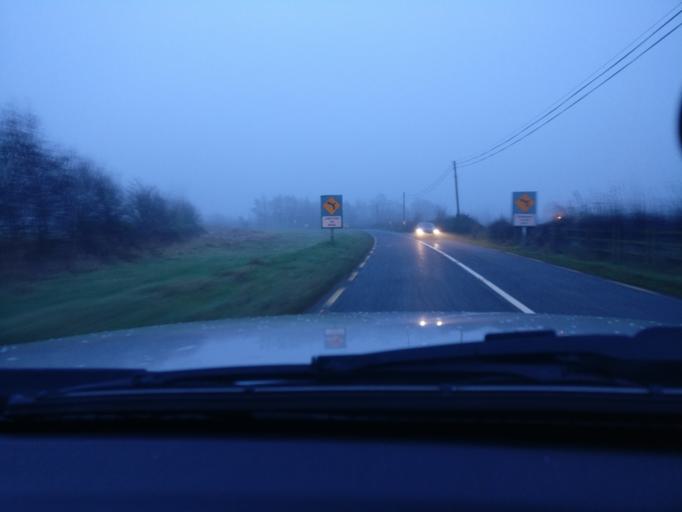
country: IE
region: Leinster
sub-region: An Mhi
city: Athboy
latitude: 53.6087
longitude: -6.9567
